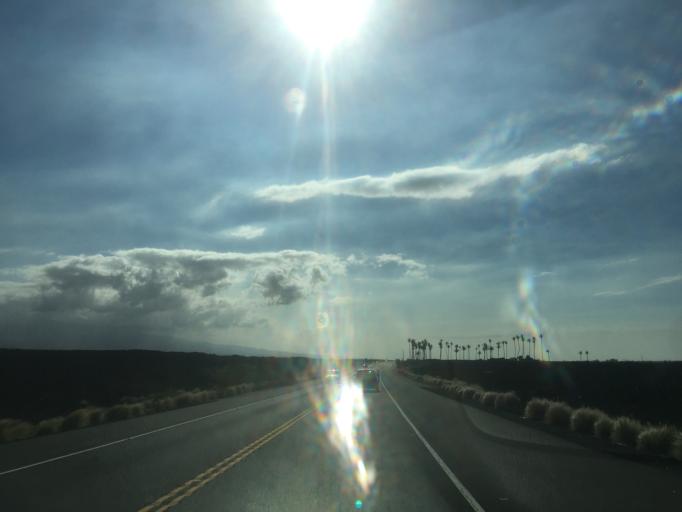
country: US
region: Hawaii
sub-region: Hawaii County
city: Waikoloa Village
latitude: 19.9378
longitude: -155.8404
